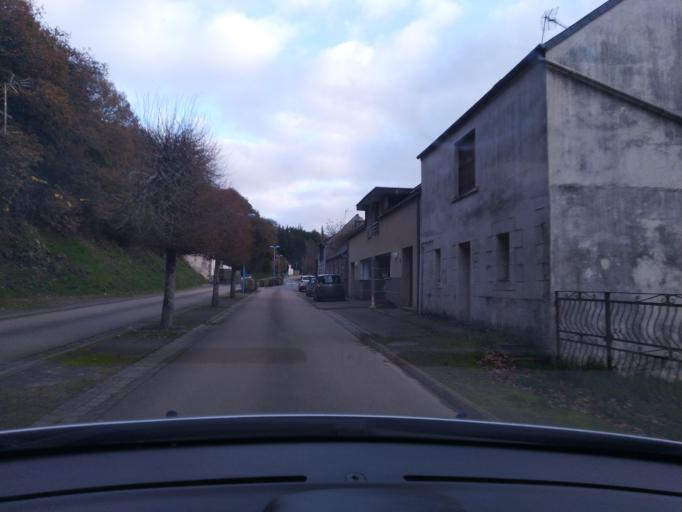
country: FR
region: Brittany
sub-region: Departement du Finistere
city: Plouigneau
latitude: 48.5648
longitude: -3.6370
